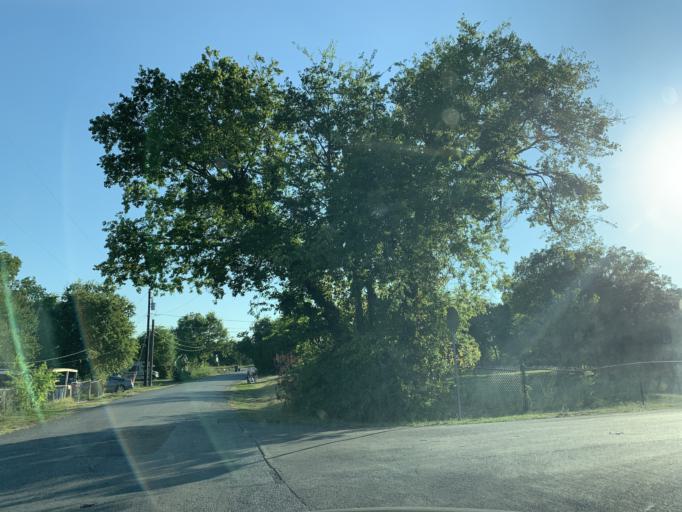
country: US
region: Texas
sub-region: Dallas County
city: Hutchins
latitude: 32.6724
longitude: -96.7789
